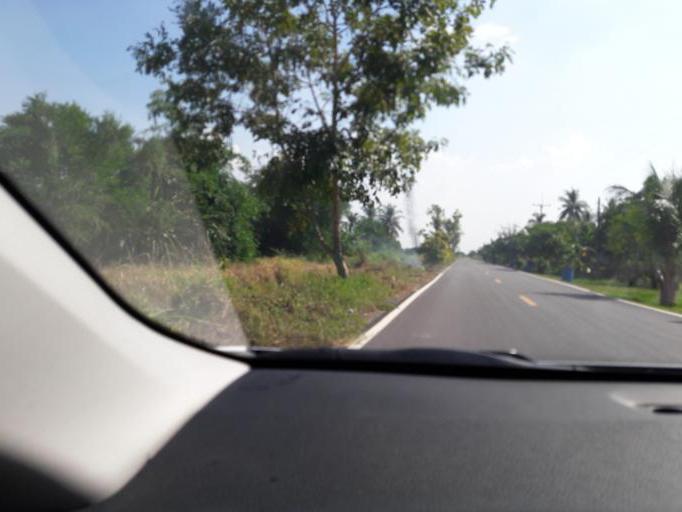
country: TH
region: Ang Thong
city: Wiset Chaichan
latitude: 14.5653
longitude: 100.3889
